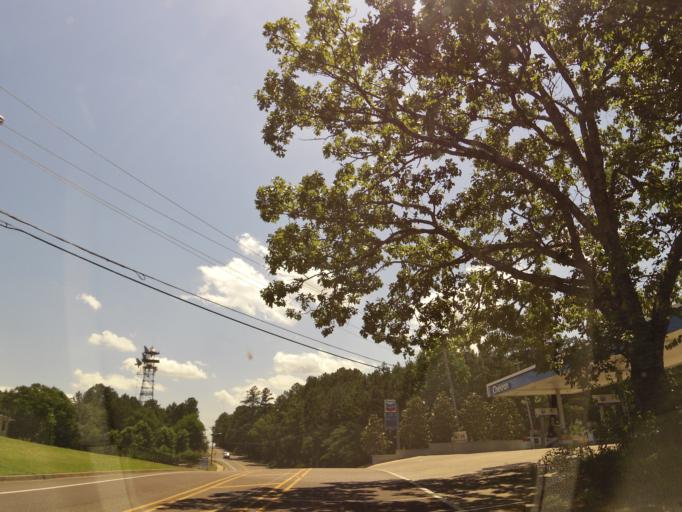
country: US
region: Mississippi
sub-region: Lafayette County
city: University
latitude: 34.3467
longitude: -89.5432
